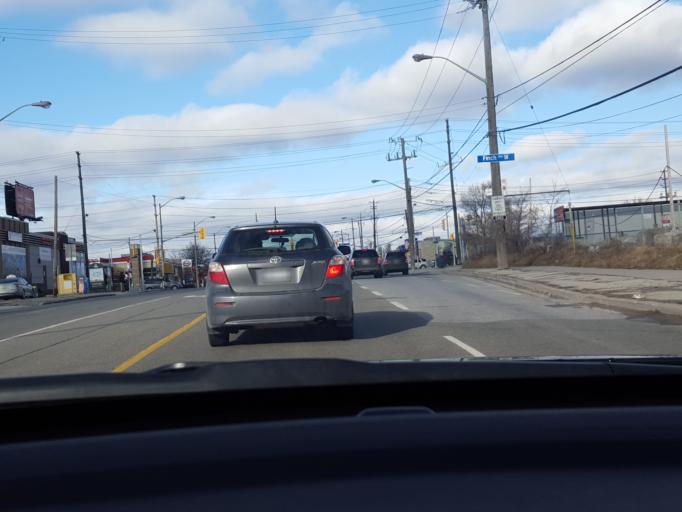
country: CA
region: Ontario
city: Concord
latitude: 43.7509
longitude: -79.5421
